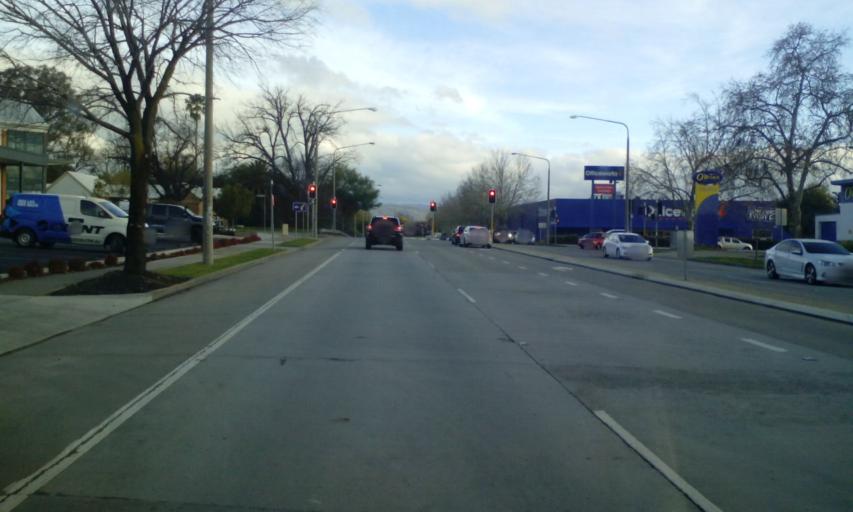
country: AU
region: New South Wales
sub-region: Albury Municipality
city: East Albury
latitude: -36.0830
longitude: 146.9234
